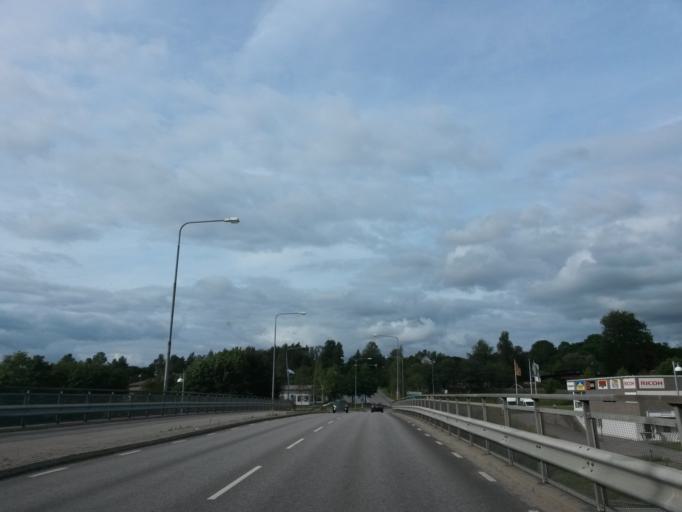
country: SE
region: Vaestra Goetaland
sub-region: Boras Kommun
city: Ganghester
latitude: 57.7239
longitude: 12.9886
